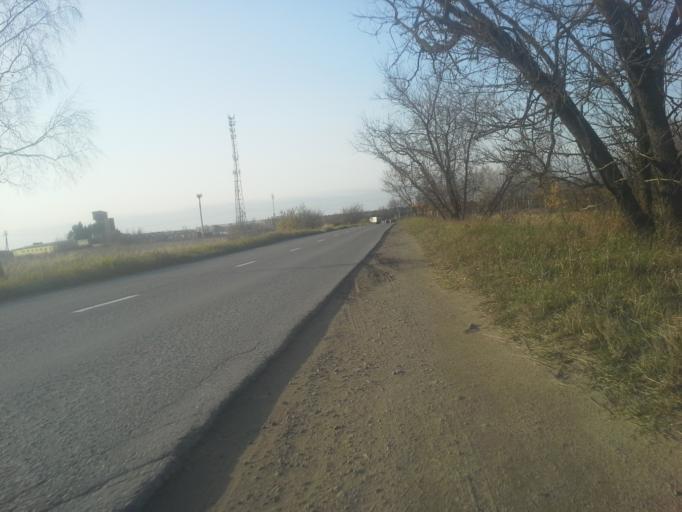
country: RU
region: Moskovskaya
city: Krasnoznamensk
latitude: 55.5942
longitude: 37.0165
